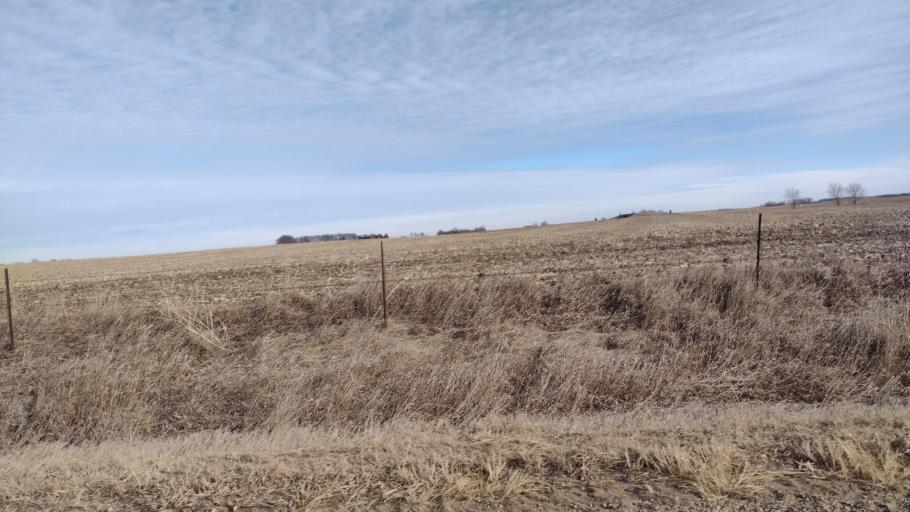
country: US
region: South Dakota
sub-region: Union County
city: Beresford
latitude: 42.9556
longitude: -96.8055
